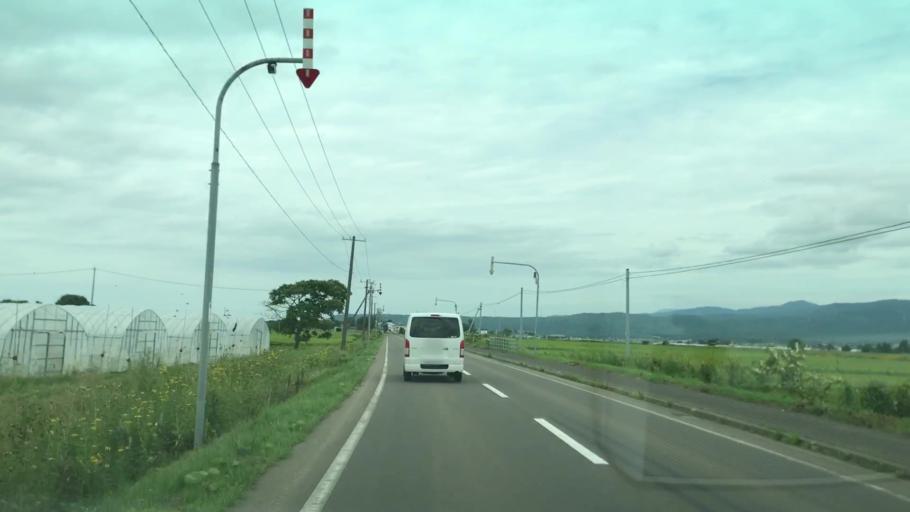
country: JP
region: Hokkaido
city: Iwanai
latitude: 42.9992
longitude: 140.5914
